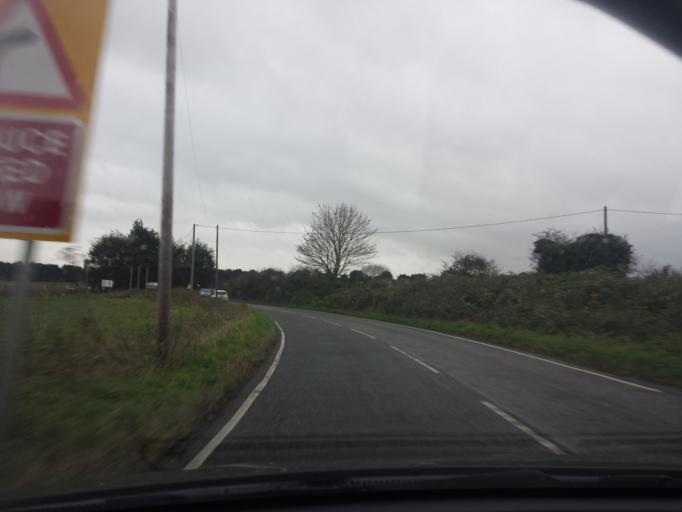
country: GB
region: England
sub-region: Essex
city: Dovercourt
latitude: 51.9070
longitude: 1.2101
